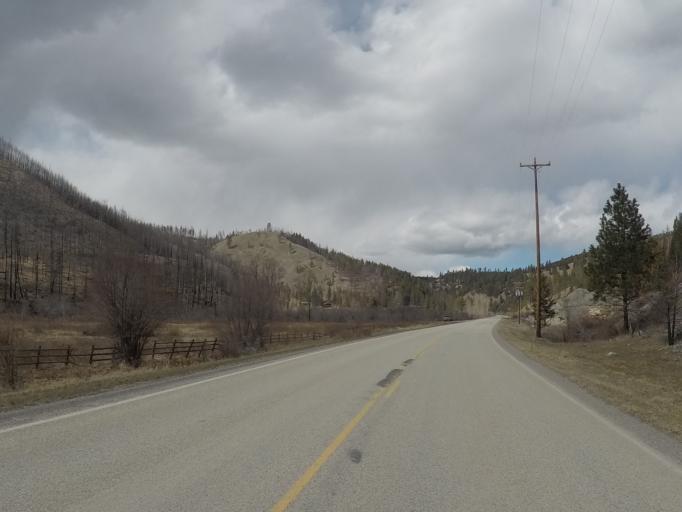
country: US
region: Montana
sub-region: Missoula County
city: Lolo
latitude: 46.7586
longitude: -114.3200
